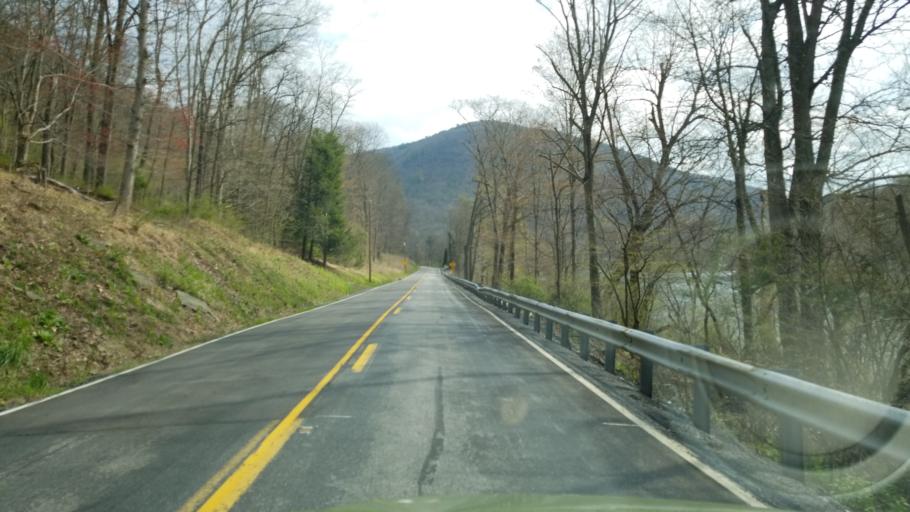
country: US
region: Pennsylvania
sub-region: Clinton County
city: Renovo
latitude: 41.2971
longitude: -78.0252
